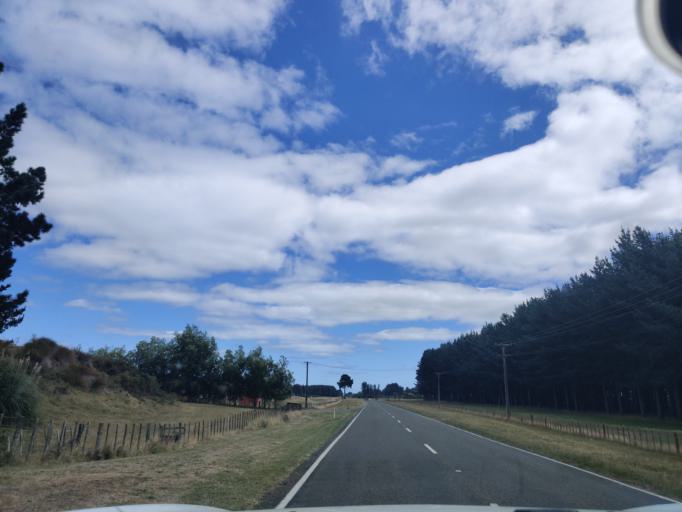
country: NZ
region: Manawatu-Wanganui
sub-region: Horowhenua District
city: Foxton
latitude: -40.4032
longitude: 175.3660
